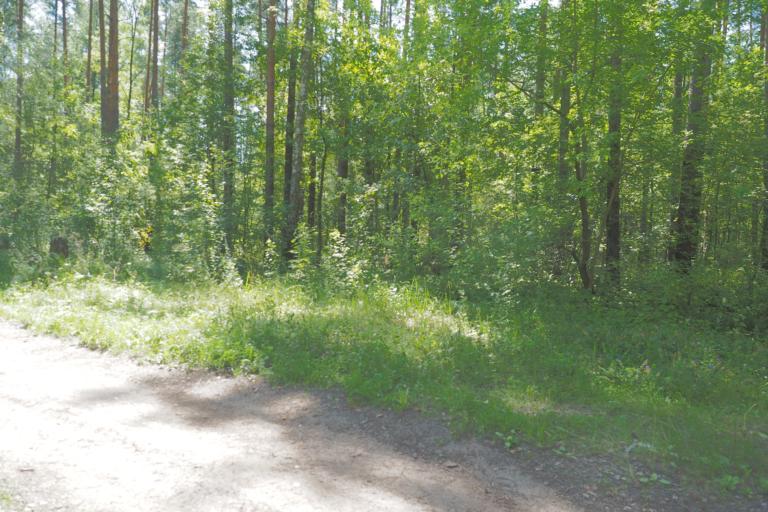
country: RU
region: Moskovskaya
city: Malyshevo
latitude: 55.5277
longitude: 38.3519
